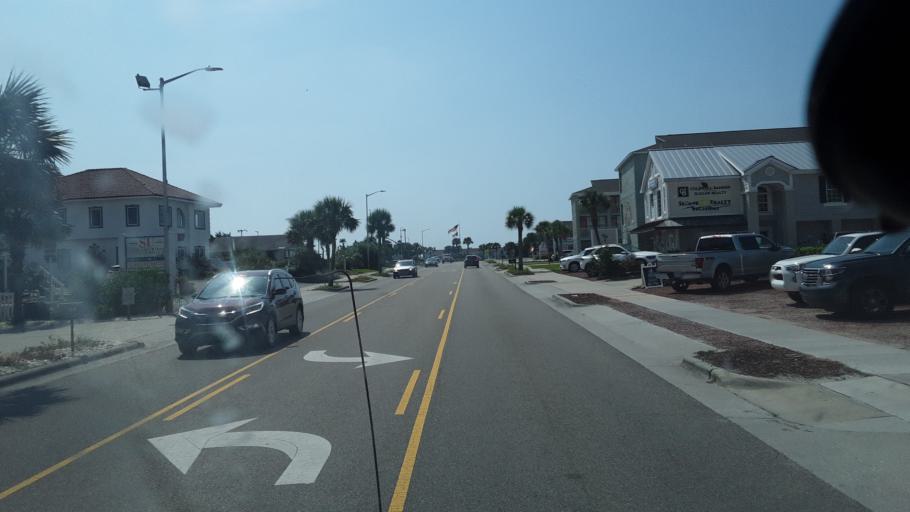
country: US
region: North Carolina
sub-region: Brunswick County
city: Sunset Beach
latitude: 33.8900
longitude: -78.4376
